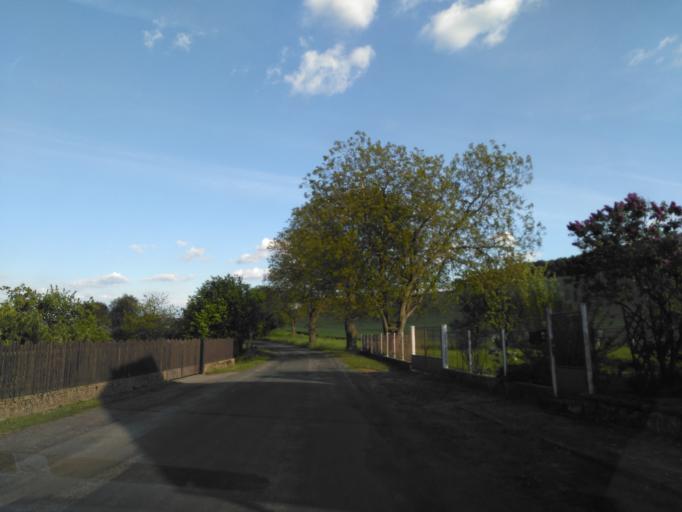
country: CZ
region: Central Bohemia
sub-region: Okres Beroun
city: Beroun
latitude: 49.8908
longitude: 14.0990
